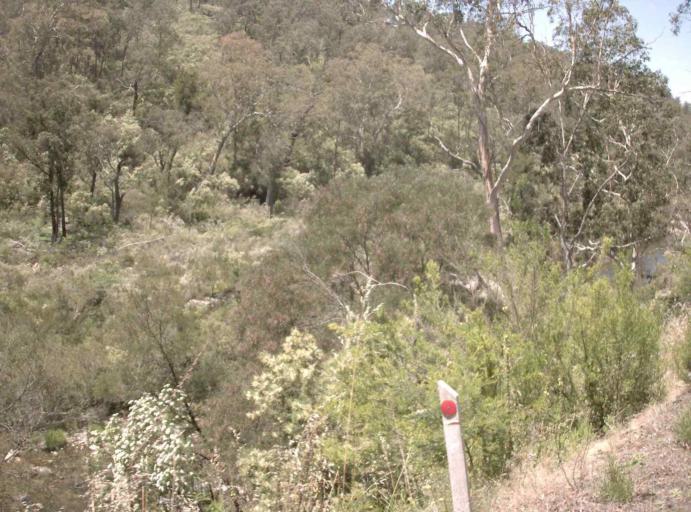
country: AU
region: Victoria
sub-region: East Gippsland
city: Bairnsdale
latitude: -37.4860
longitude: 147.8328
